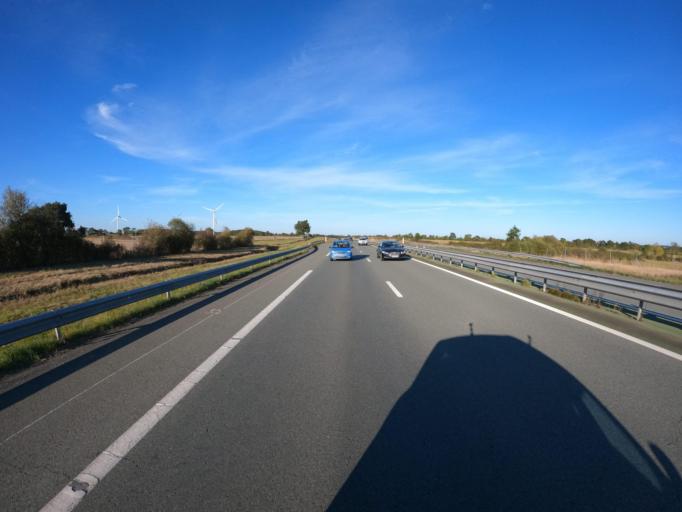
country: FR
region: Pays de la Loire
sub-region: Departement de Maine-et-Loire
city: Trementines
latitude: 47.1797
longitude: -0.7845
